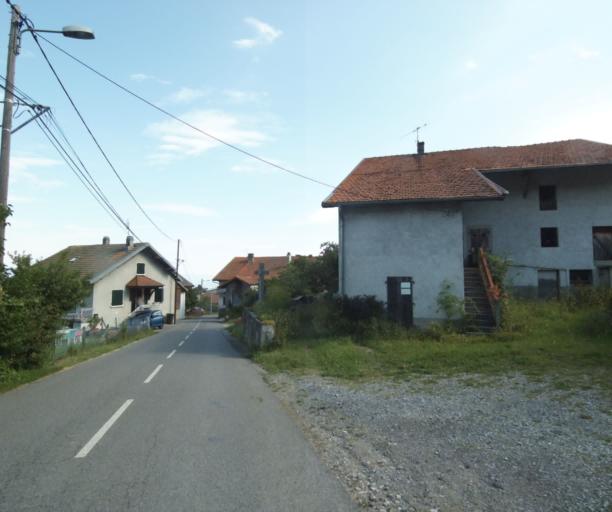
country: FR
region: Rhone-Alpes
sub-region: Departement de la Haute-Savoie
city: Lyaud
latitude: 46.3161
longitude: 6.5104
